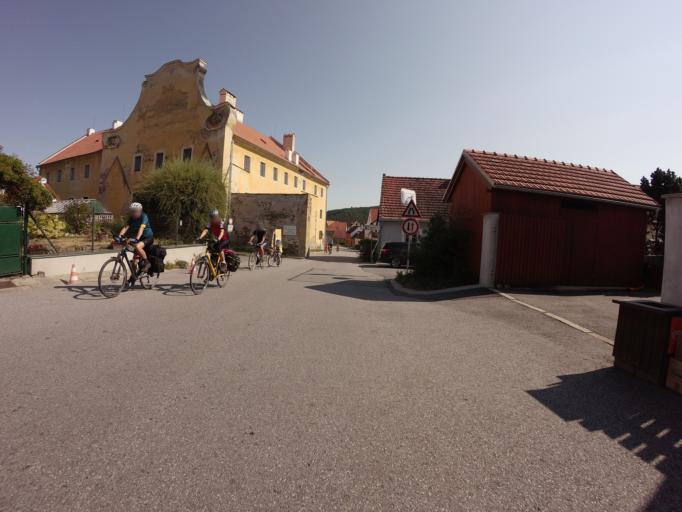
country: CZ
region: Jihocesky
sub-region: Okres Cesky Krumlov
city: Cesky Krumlov
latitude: 48.8535
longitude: 14.3678
